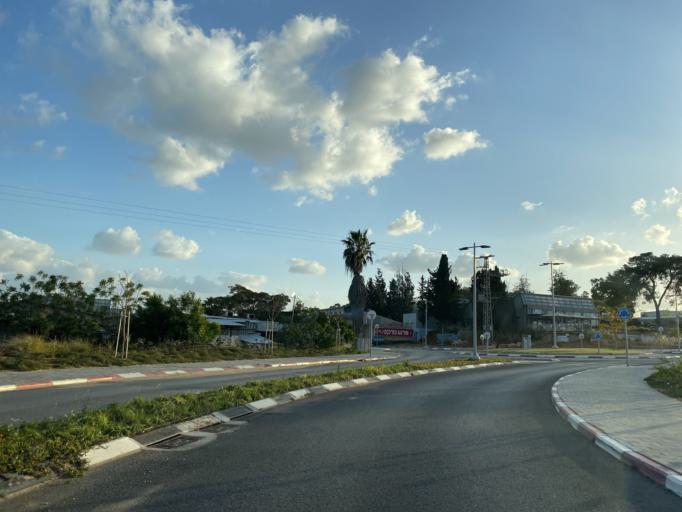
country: IL
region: Tel Aviv
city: Herzliyya
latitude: 32.1597
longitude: 34.8339
